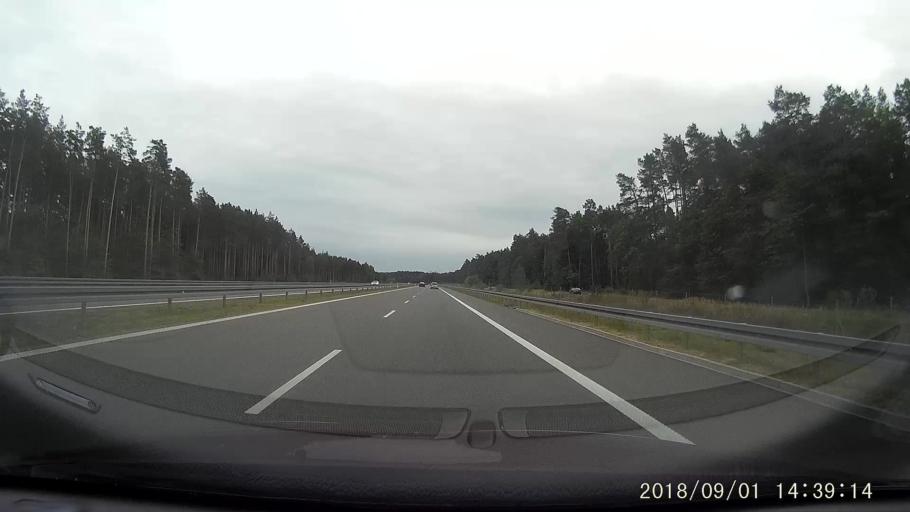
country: PL
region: West Pomeranian Voivodeship
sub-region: Powiat mysliborski
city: Nowogrodek Pomorski
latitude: 52.8218
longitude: 15.0758
